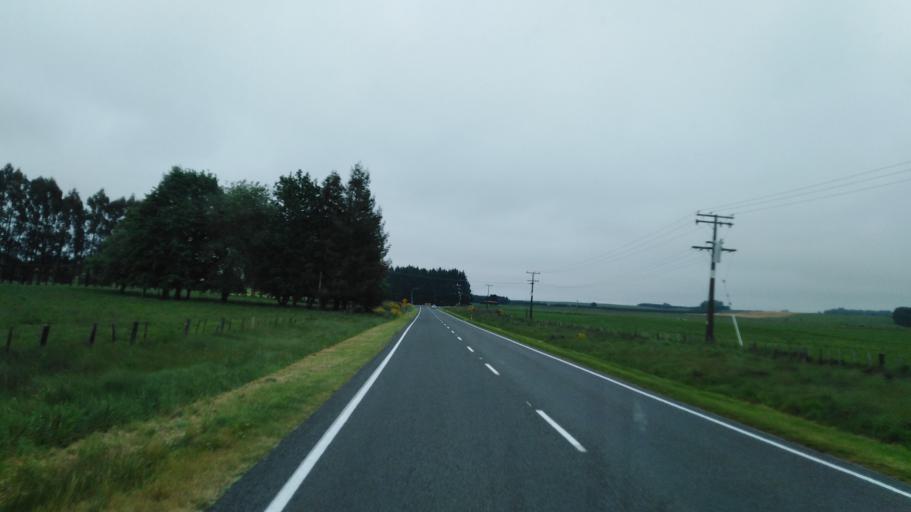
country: NZ
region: Waikato
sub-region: Taupo District
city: Taupo
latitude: -38.6563
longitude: 176.1610
